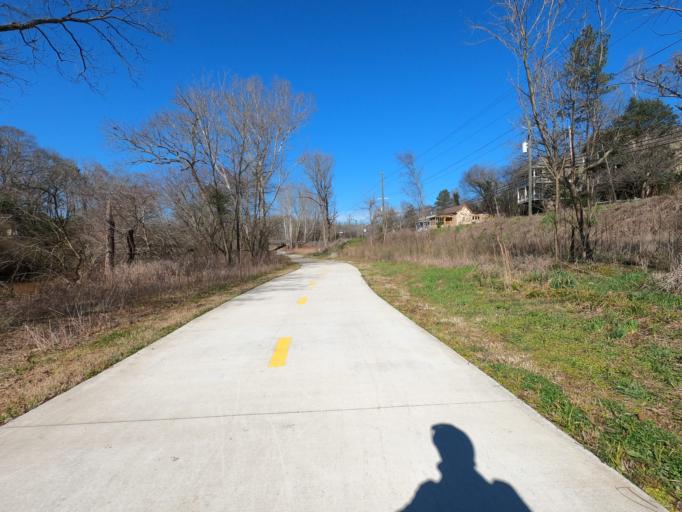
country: US
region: Georgia
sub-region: Clarke County
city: Athens
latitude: 33.9694
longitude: -83.3760
